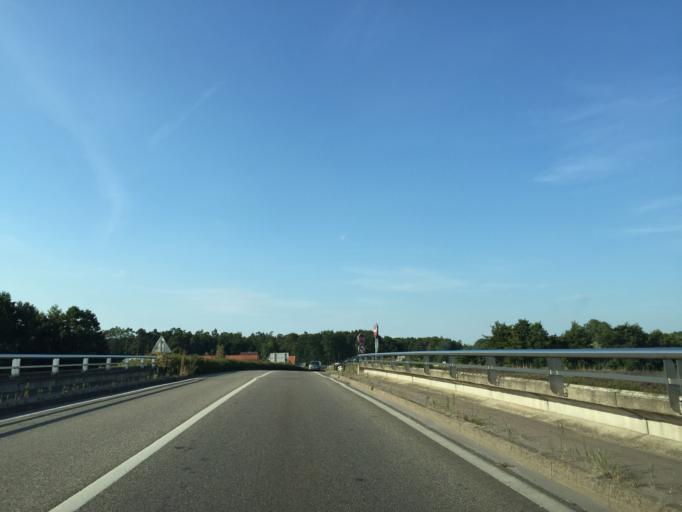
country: FR
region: Alsace
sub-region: Departement du Bas-Rhin
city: Haguenau
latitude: 48.8331
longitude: 7.7996
